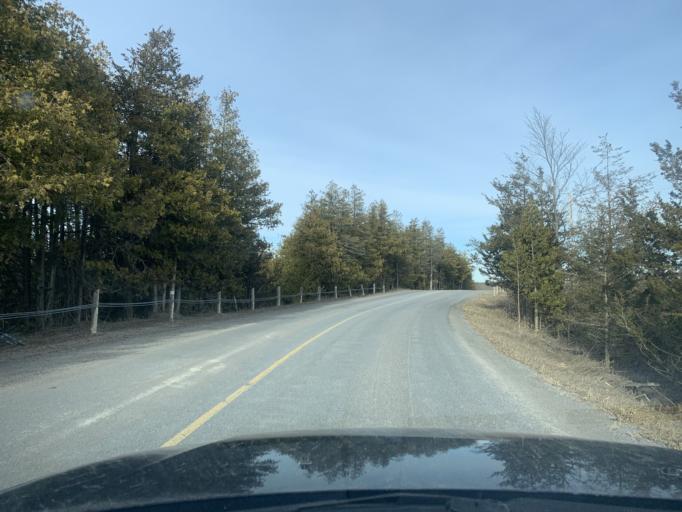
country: CA
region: Ontario
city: Deseronto
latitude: 44.4219
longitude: -77.1024
